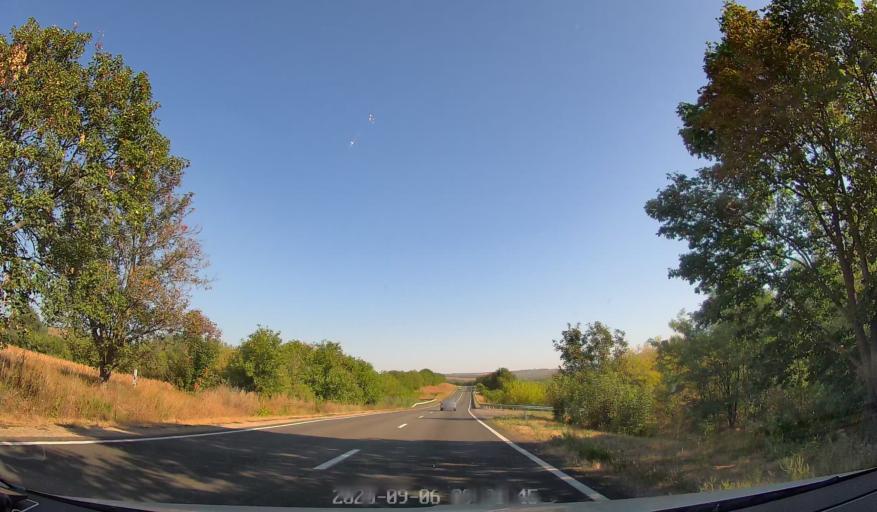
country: MD
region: Orhei
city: Orhei
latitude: 47.4836
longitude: 28.7941
